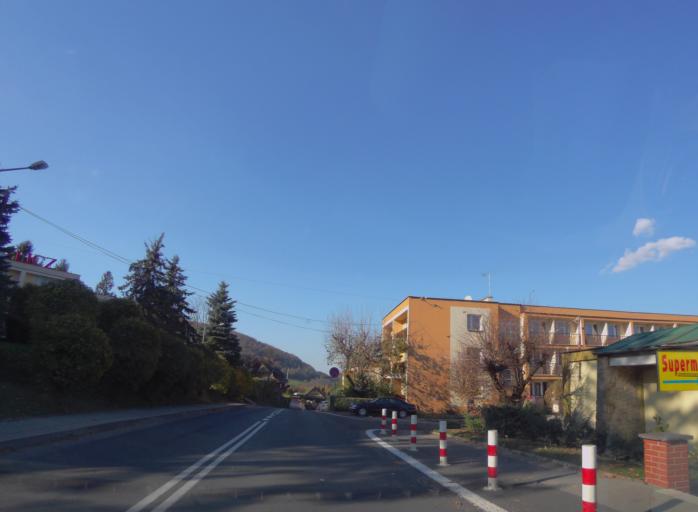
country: PL
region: Subcarpathian Voivodeship
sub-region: Powiat leski
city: Polanczyk
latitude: 49.4004
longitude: 22.4495
